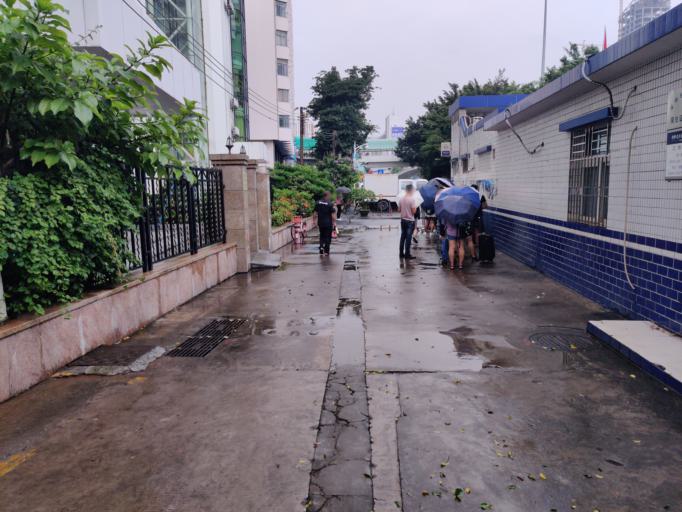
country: CN
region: Guangdong
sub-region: Shenzhen
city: Shenzhen
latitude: 22.5305
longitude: 114.1115
